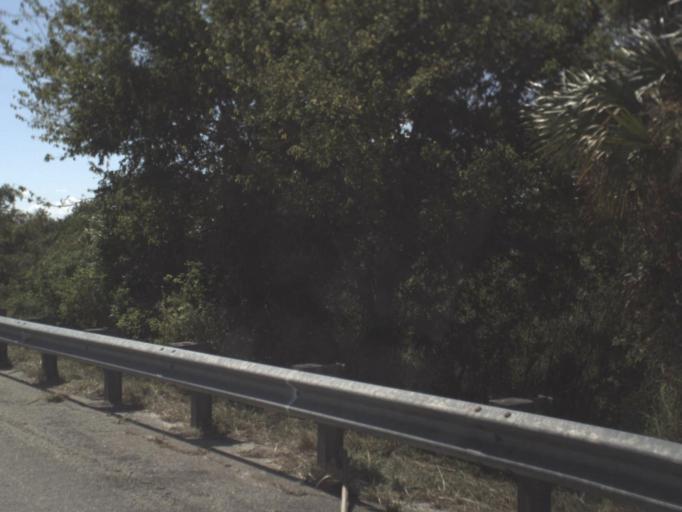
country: US
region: Florida
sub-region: Glades County
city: Buckhead Ridge
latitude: 27.0725
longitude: -80.9755
